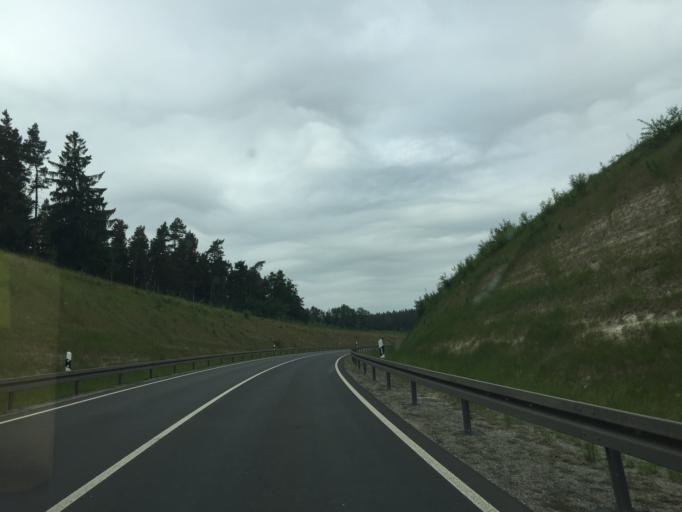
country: DE
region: Thuringia
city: Langewiesen
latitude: 50.6997
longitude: 10.9639
